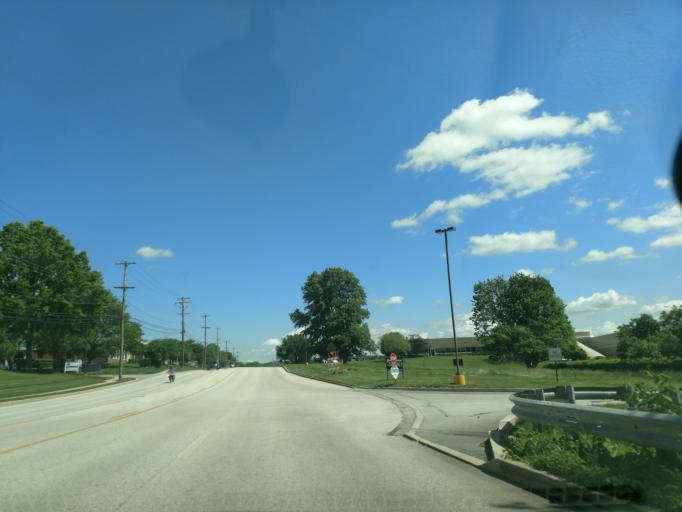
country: US
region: Pennsylvania
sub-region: Montgomery County
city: King of Prussia
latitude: 40.1007
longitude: -75.3975
